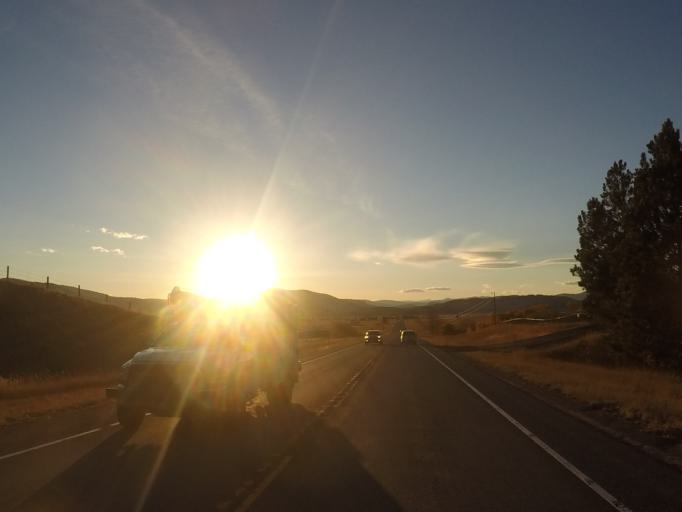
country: US
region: Montana
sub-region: Missoula County
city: Seeley Lake
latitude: 47.0201
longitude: -113.1029
